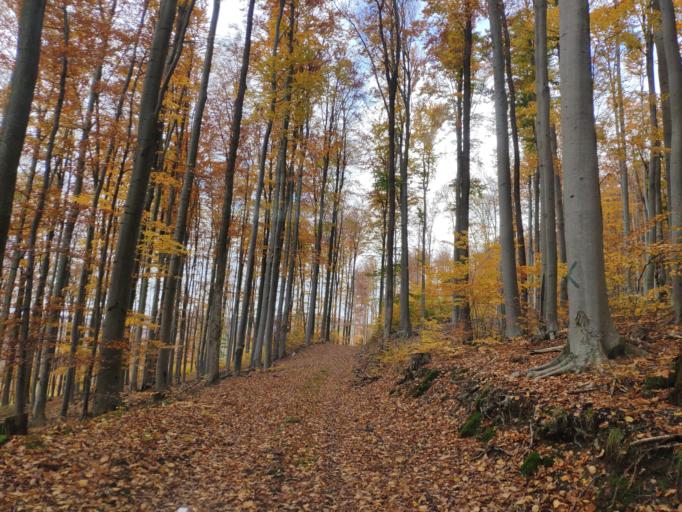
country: SK
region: Kosicky
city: Medzev
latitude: 48.7334
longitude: 20.9959
